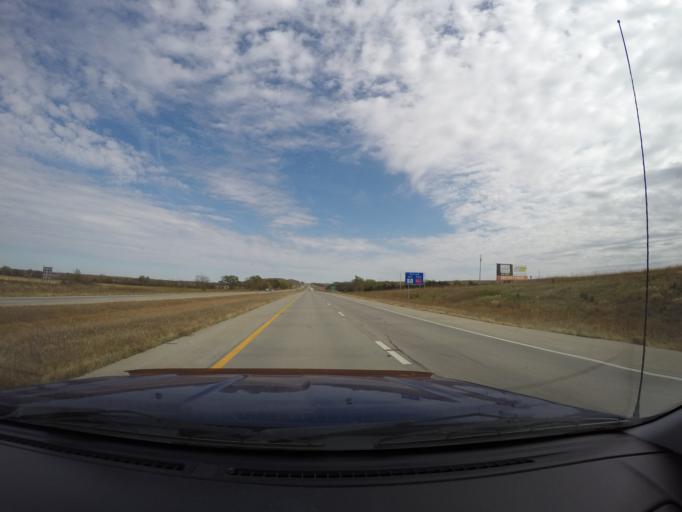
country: US
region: Kansas
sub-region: Pottawatomie County
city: Saint Marys
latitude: 39.0582
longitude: -96.1100
